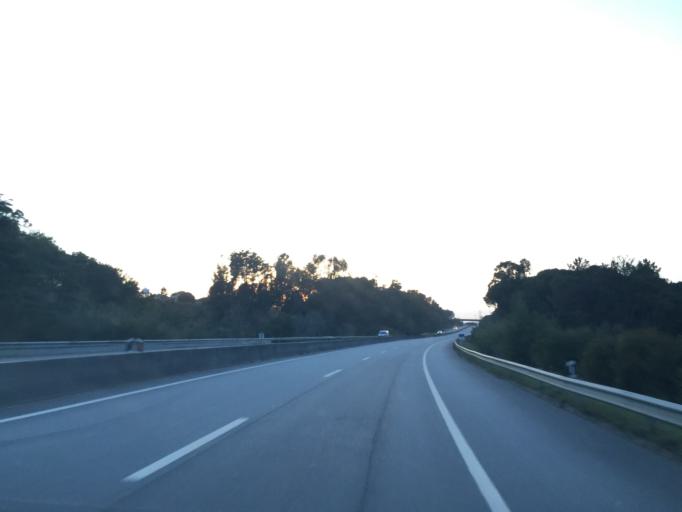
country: PT
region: Viseu
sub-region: Concelho de Carregal do Sal
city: Carregal do Sal
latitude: 40.4390
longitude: -7.9927
